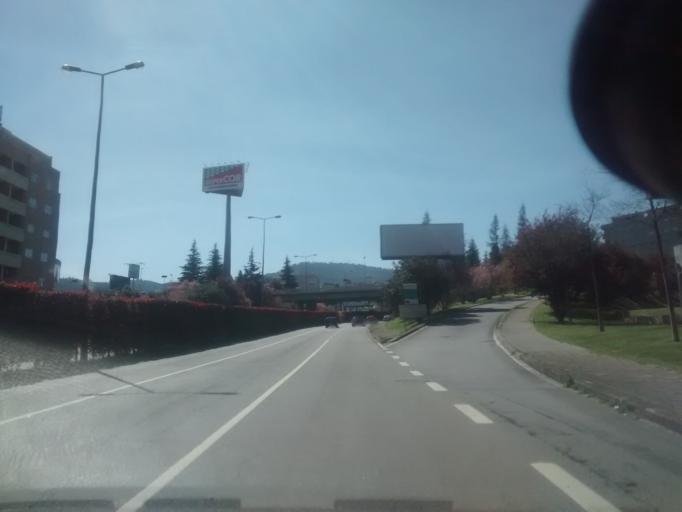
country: PT
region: Braga
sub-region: Braga
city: Braga
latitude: 41.5430
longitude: -8.4039
